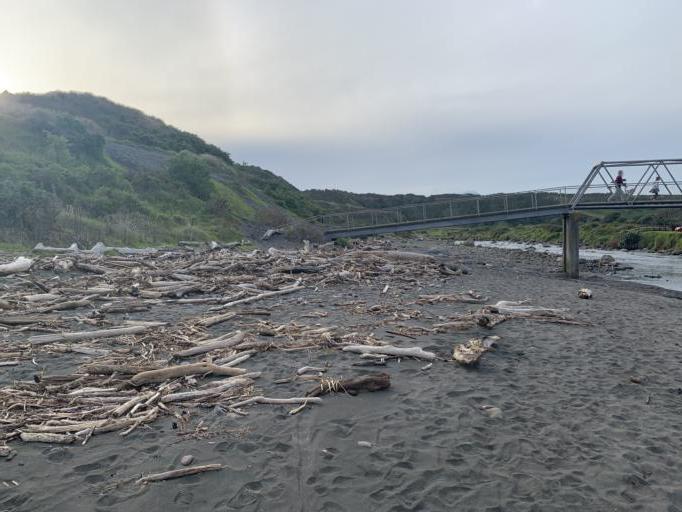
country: NZ
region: Taranaki
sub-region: South Taranaki District
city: Hawera
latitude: -39.5657
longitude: 174.0607
